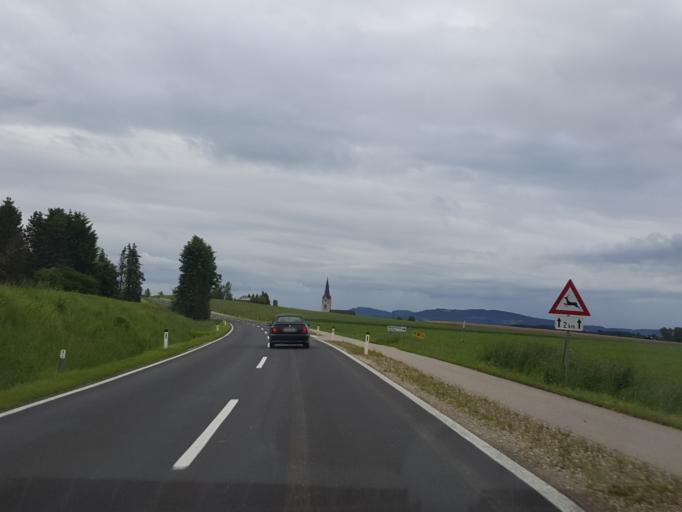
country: AT
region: Upper Austria
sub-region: Politischer Bezirk Vocklabruck
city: Gampern
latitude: 47.9806
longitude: 13.5595
